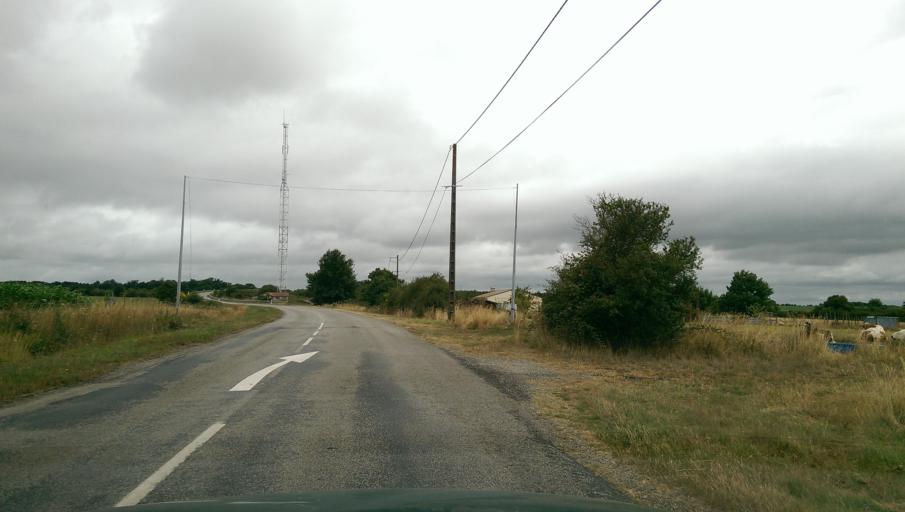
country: FR
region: Pays de la Loire
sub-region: Departement de la Loire-Atlantique
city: La Planche
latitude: 47.0258
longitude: -1.4066
